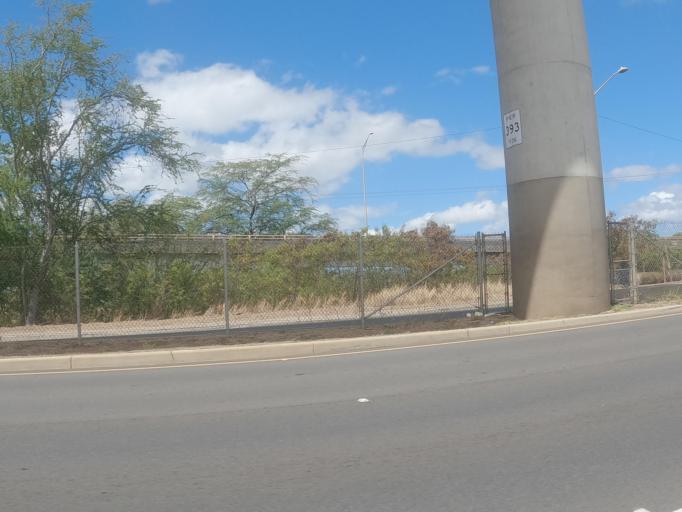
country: US
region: Hawaii
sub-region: Honolulu County
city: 'Aiea
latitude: 21.3770
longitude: -157.9340
